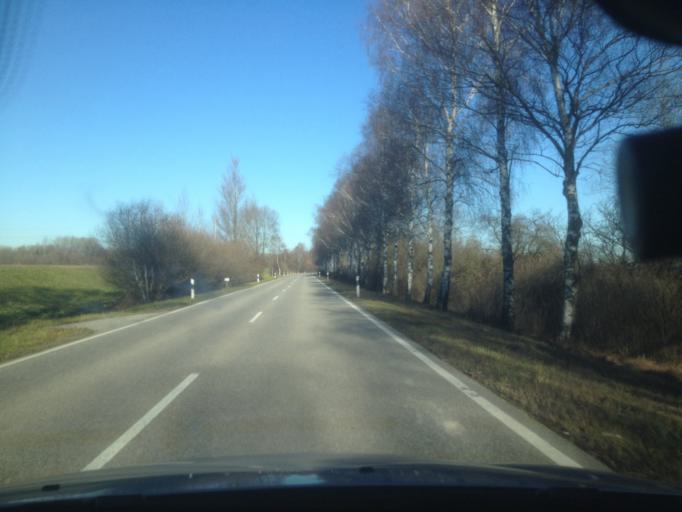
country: DE
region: Bavaria
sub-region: Upper Bavaria
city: Langenpreising
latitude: 48.4304
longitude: 11.9356
